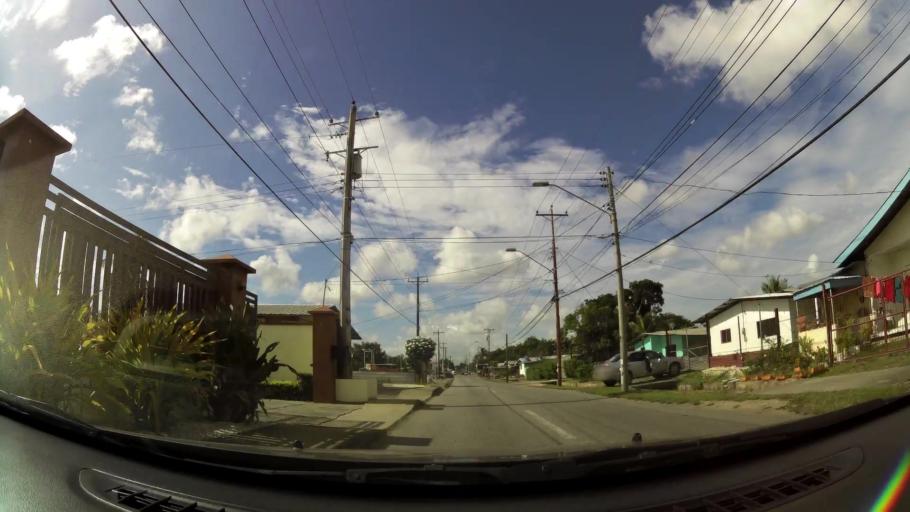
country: TT
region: Chaguanas
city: Chaguanas
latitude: 10.5334
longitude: -61.4015
